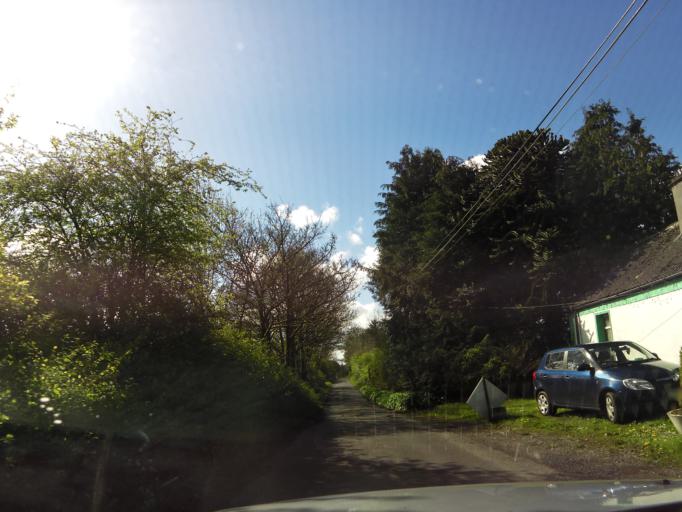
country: IE
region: Connaught
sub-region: Maigh Eo
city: Kiltamagh
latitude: 53.7934
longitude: -8.9650
